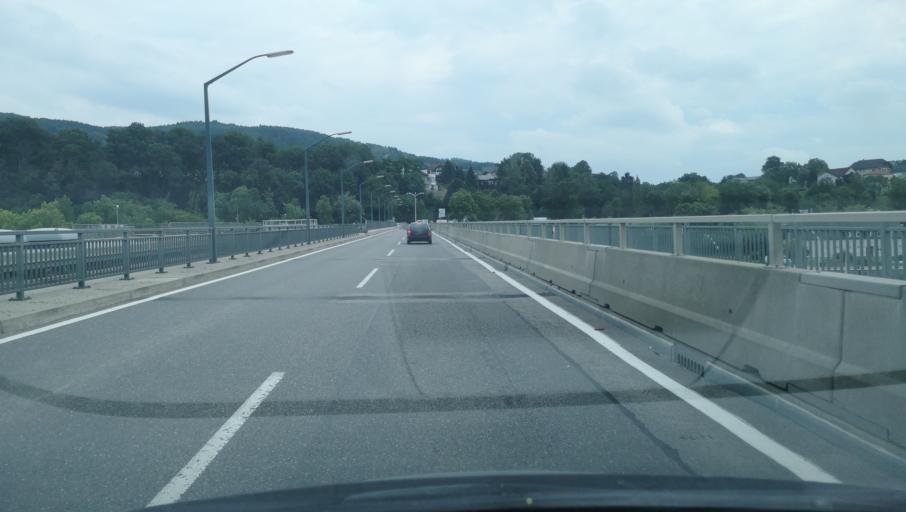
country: AT
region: Lower Austria
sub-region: Politischer Bezirk Melk
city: Ybbs an der Donau
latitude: 48.1908
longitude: 15.0710
